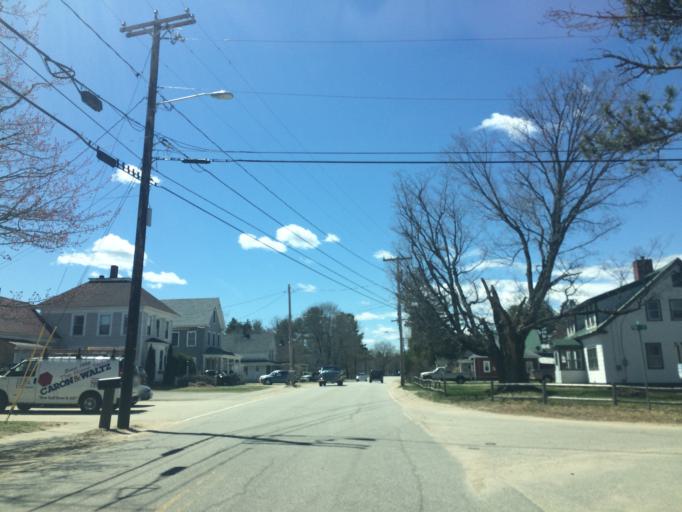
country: US
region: Maine
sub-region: Oxford County
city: Porter
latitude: 43.8118
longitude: -70.8826
